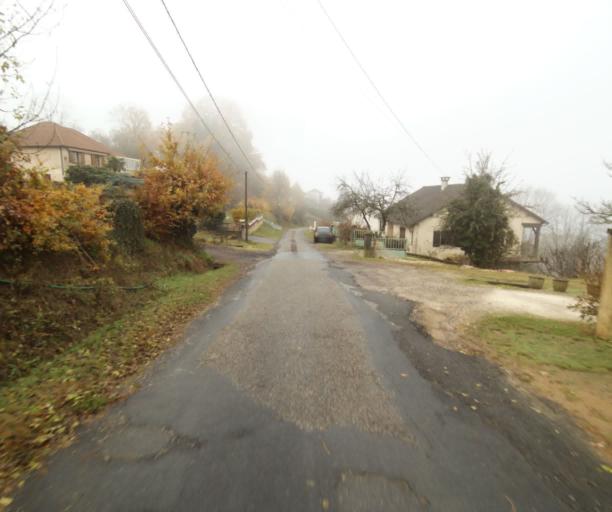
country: FR
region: Limousin
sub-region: Departement de la Correze
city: Sainte-Fereole
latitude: 45.1860
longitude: 1.6191
